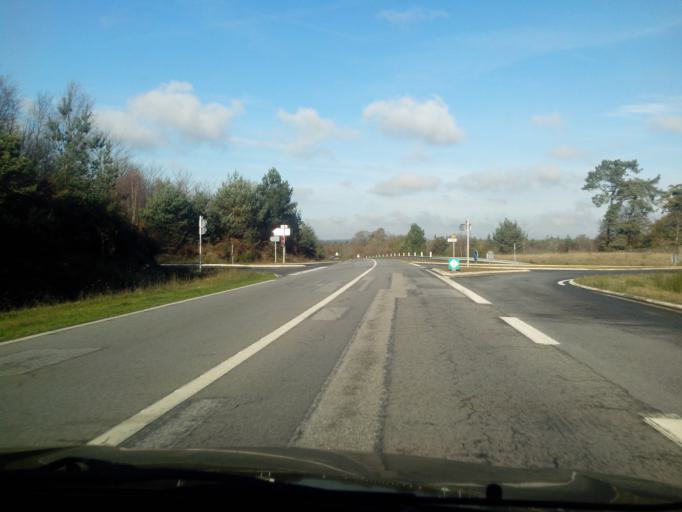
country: FR
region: Brittany
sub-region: Departement du Morbihan
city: Molac
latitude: 47.7531
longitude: -2.4388
